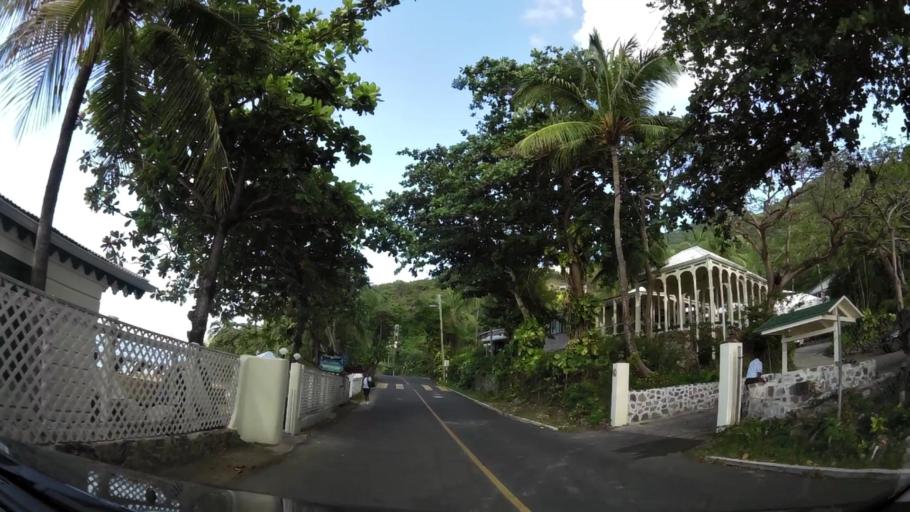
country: VG
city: Road Town
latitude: 18.4019
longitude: -64.6772
